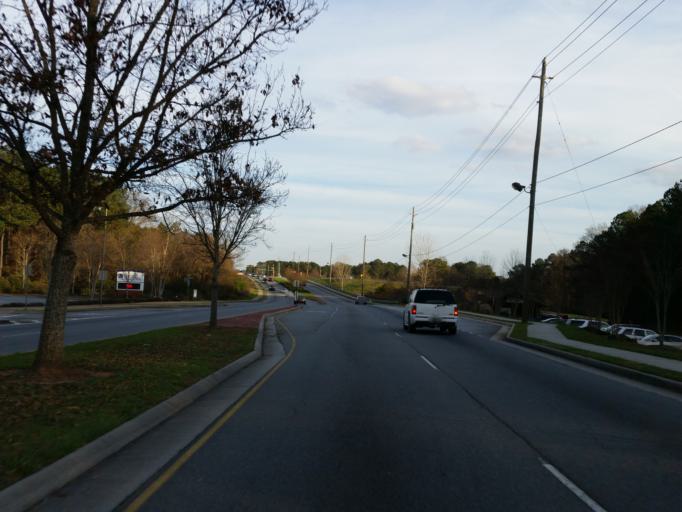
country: US
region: Georgia
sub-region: Cobb County
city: Powder Springs
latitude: 33.8617
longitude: -84.6718
